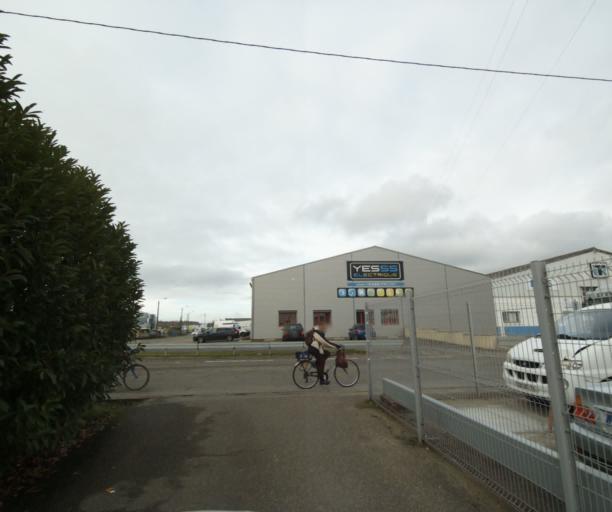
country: FR
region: Pays de la Loire
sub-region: Departement de la Sarthe
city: Allonnes
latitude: 47.9682
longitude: 0.1739
